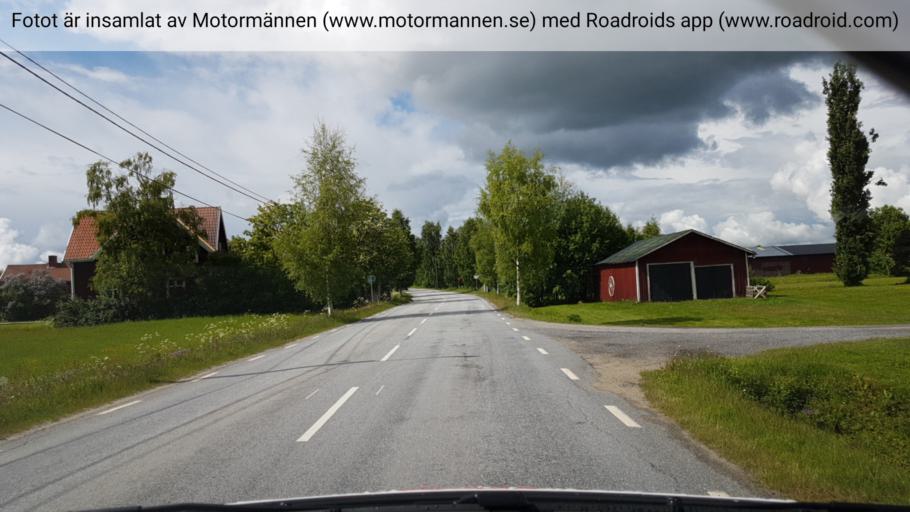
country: SE
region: Vaesterbotten
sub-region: Vannas Kommun
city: Vannasby
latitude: 63.9120
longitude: 19.8504
